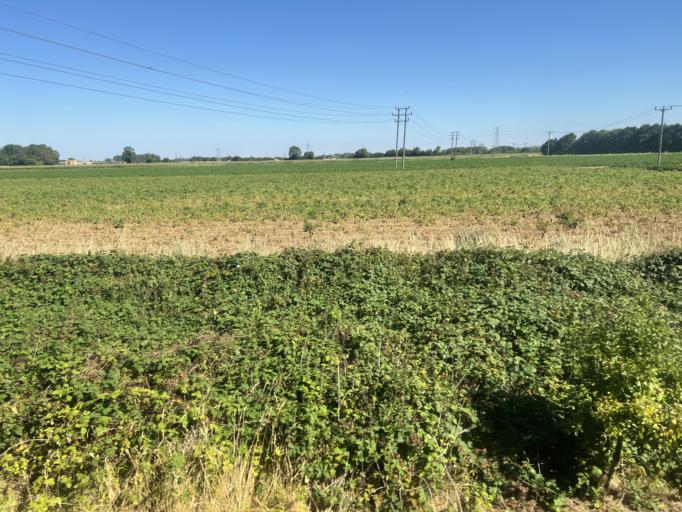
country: GB
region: England
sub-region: Lincolnshire
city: Sleaford
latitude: 52.9931
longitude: -0.3775
